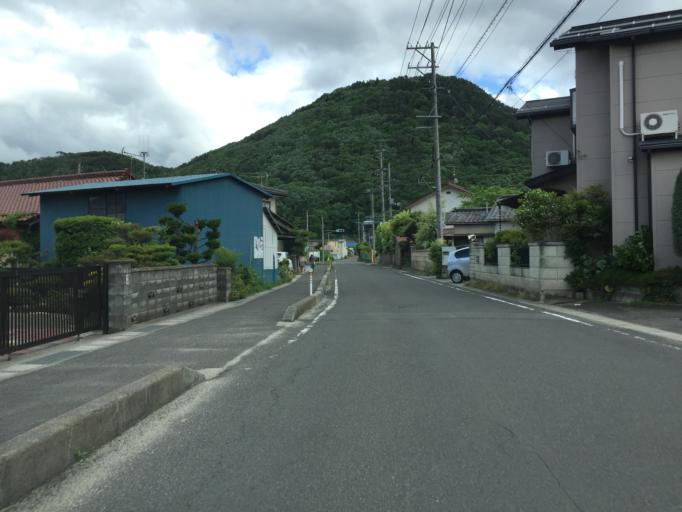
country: JP
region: Fukushima
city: Fukushima-shi
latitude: 37.7769
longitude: 140.4587
